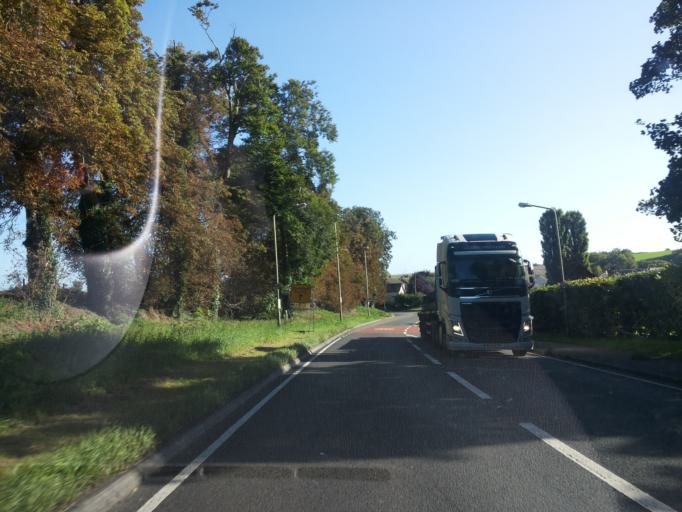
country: GB
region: England
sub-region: Wiltshire
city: Winterbourne Stoke
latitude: 51.1677
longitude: -1.8957
